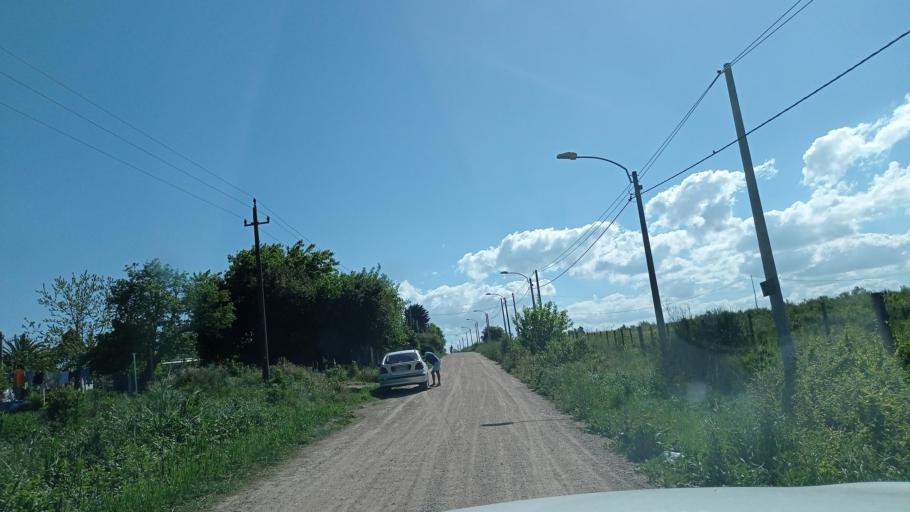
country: UY
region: Canelones
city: Toledo
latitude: -34.7803
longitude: -56.1564
